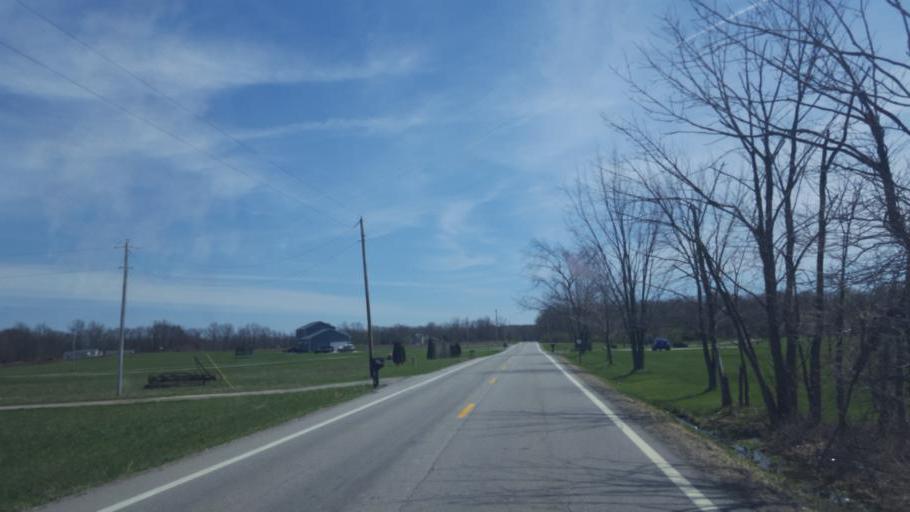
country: US
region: Ohio
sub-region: Delaware County
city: Ashley
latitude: 40.4201
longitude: -83.0283
